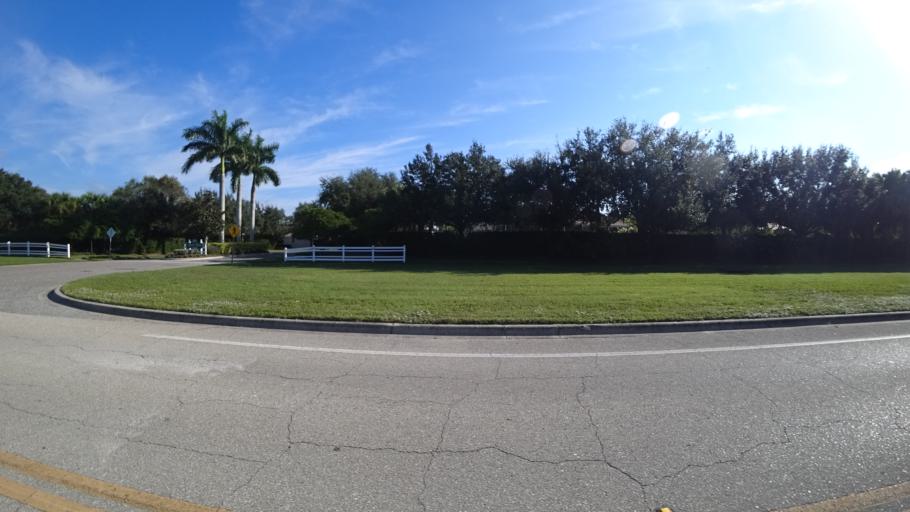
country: US
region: Florida
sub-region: Sarasota County
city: Desoto Lakes
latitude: 27.4239
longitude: -82.4836
